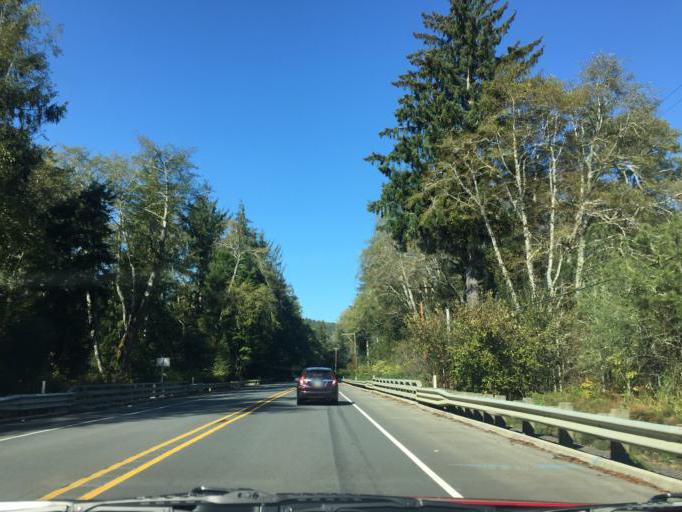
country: US
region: Oregon
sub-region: Clatsop County
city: Cannon Beach
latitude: 45.9066
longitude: -123.8805
